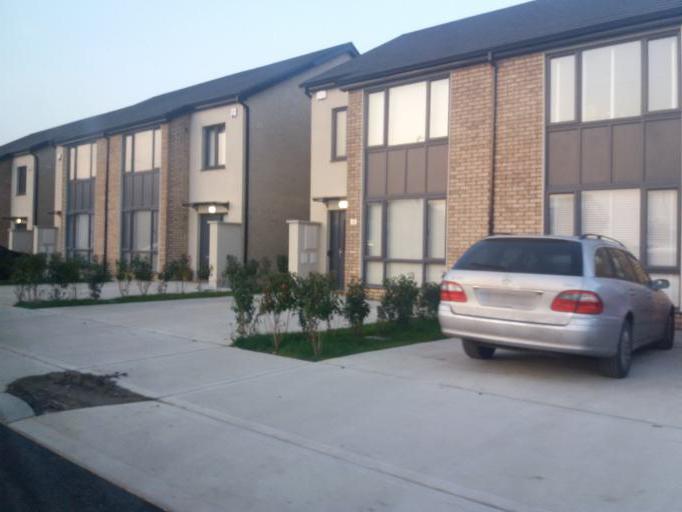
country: IE
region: Leinster
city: Hartstown
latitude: 53.3894
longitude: -6.4359
